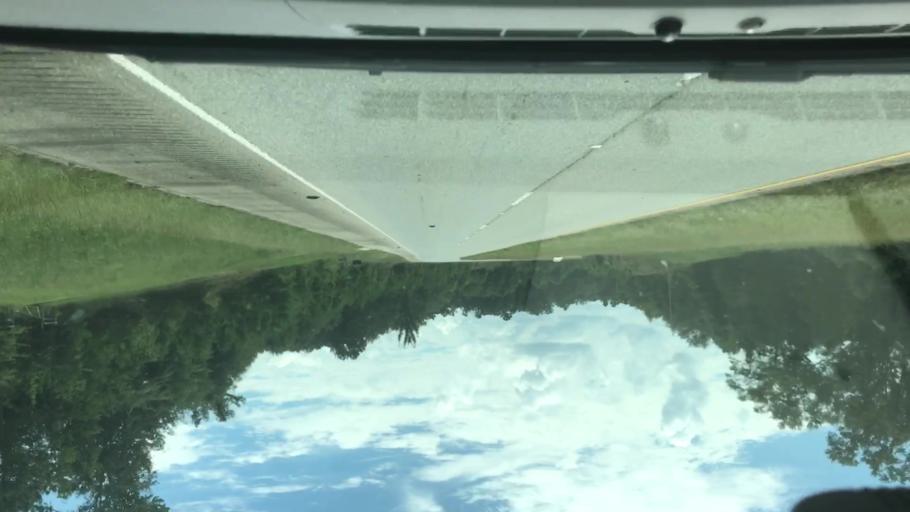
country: US
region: Georgia
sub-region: Stewart County
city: Lumpkin
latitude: 32.1647
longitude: -84.8305
